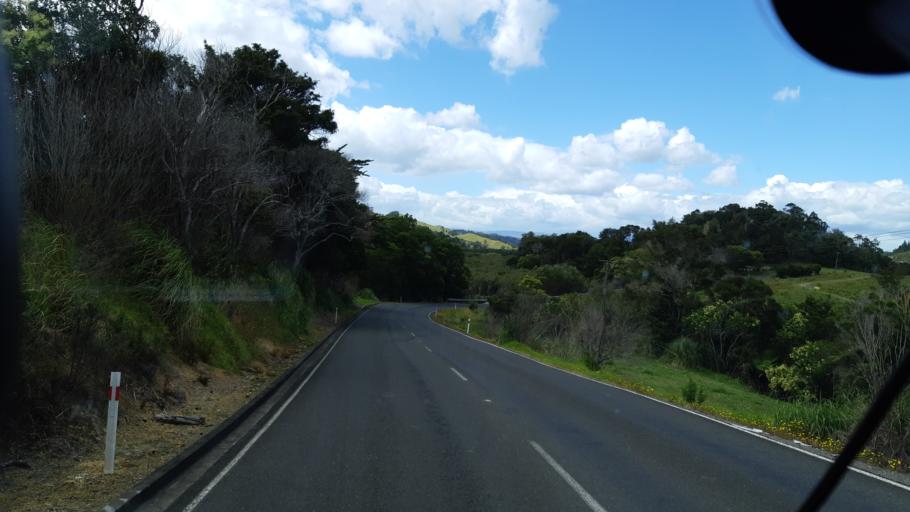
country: NZ
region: Northland
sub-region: Far North District
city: Taipa
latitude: -35.2658
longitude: 173.5243
